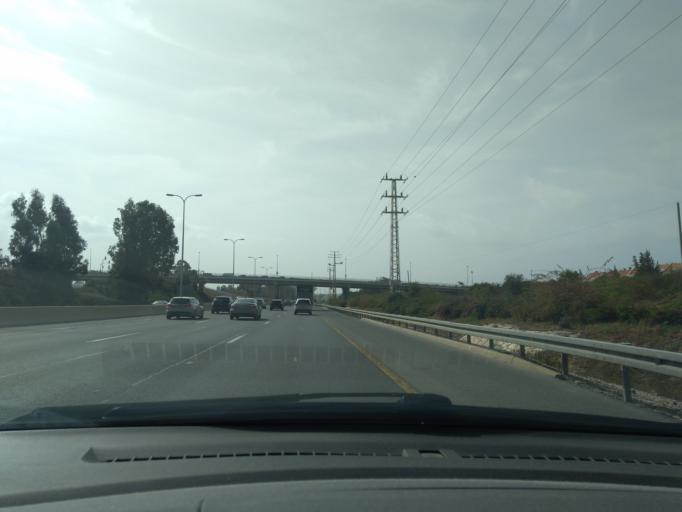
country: IL
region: Central District
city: Netanya
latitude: 32.3141
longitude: 34.8657
